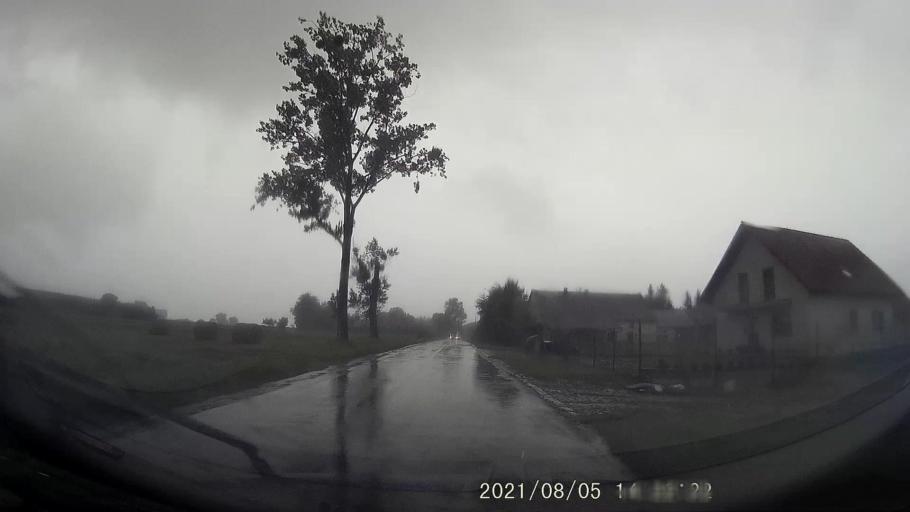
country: PL
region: Opole Voivodeship
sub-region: Powiat nyski
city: Korfantow
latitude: 50.4766
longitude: 17.6578
